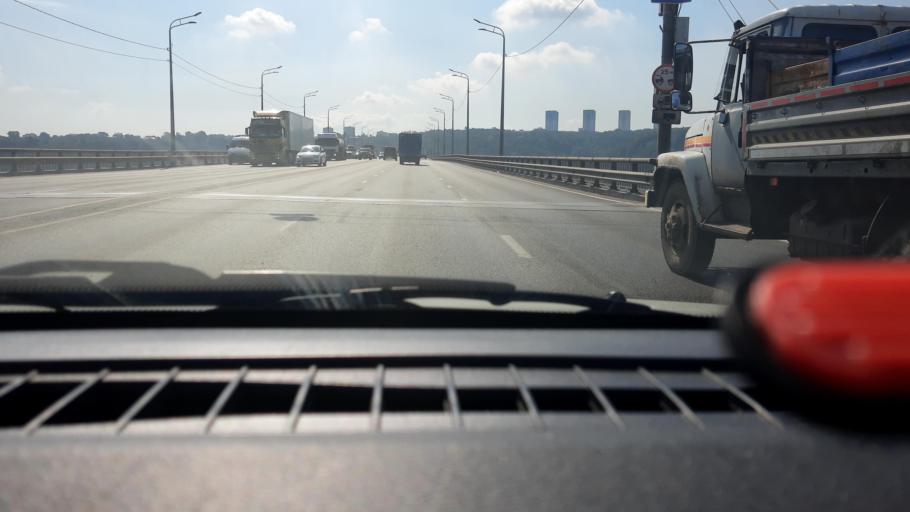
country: RU
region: Nizjnij Novgorod
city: Nizhniy Novgorod
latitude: 56.2545
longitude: 43.9426
